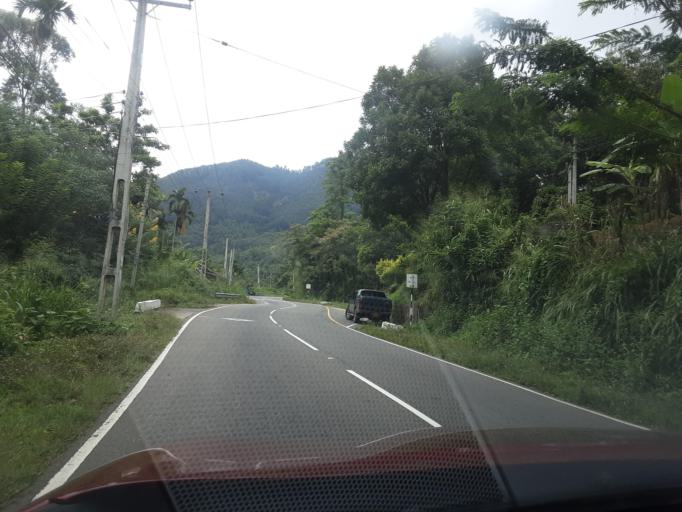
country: LK
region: Uva
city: Badulla
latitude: 6.9366
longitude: 81.1943
